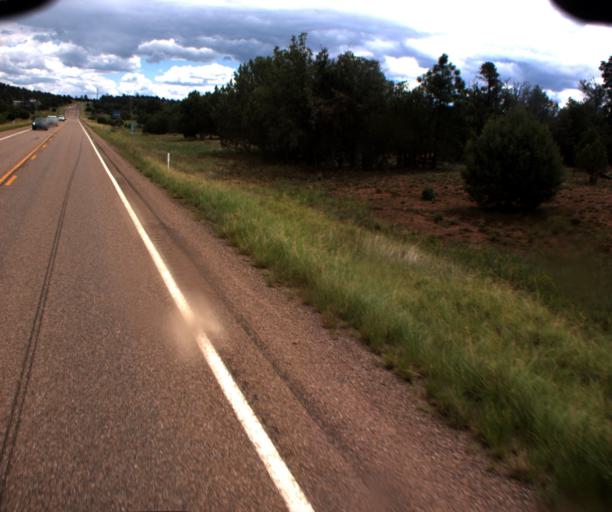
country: US
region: Arizona
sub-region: Navajo County
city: Linden
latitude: 34.3448
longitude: -110.2930
